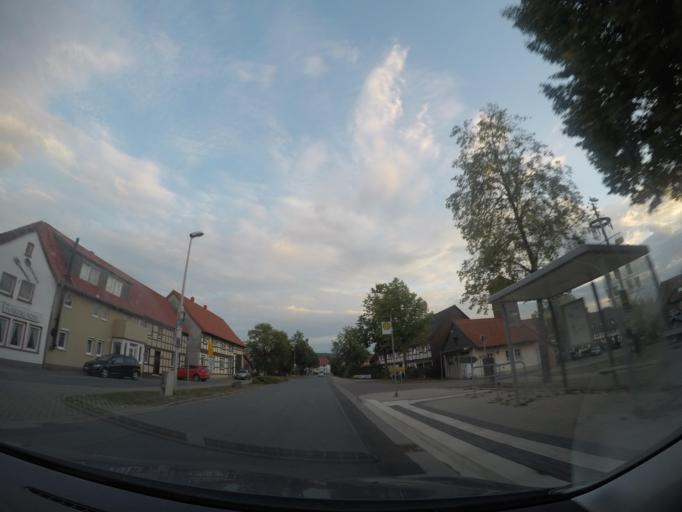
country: DE
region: Lower Saxony
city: Seesen
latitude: 51.8499
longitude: 10.1803
